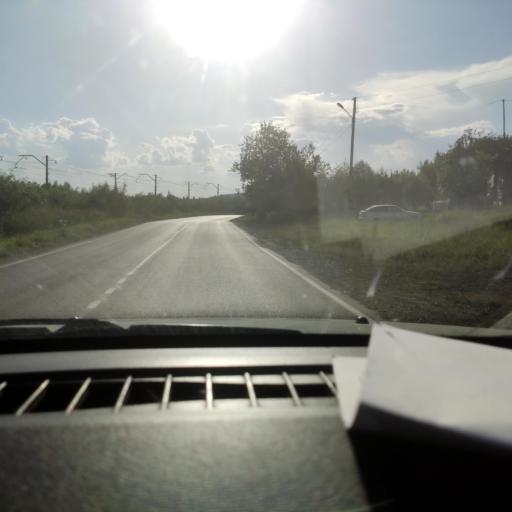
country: RU
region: Perm
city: Krasnokamsk
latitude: 58.1338
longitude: 55.7478
